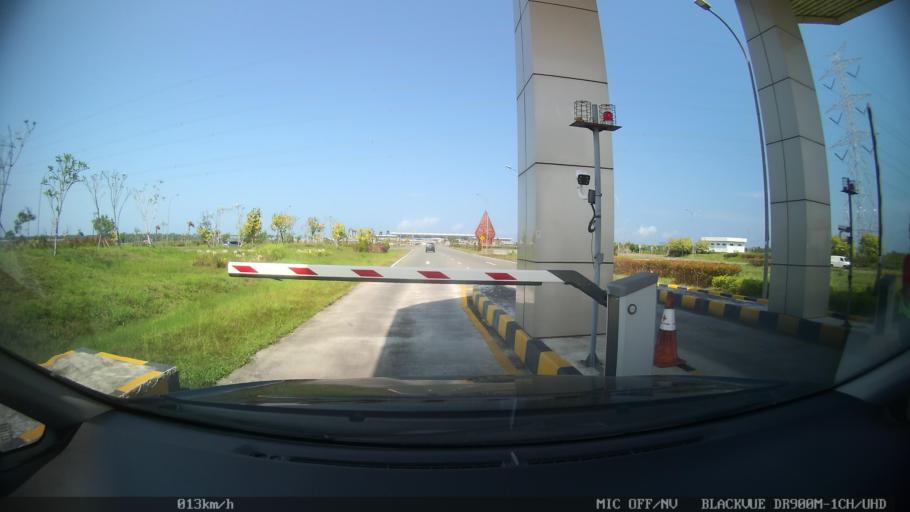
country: ID
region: Daerah Istimewa Yogyakarta
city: Srandakan
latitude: -7.8892
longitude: 110.0633
